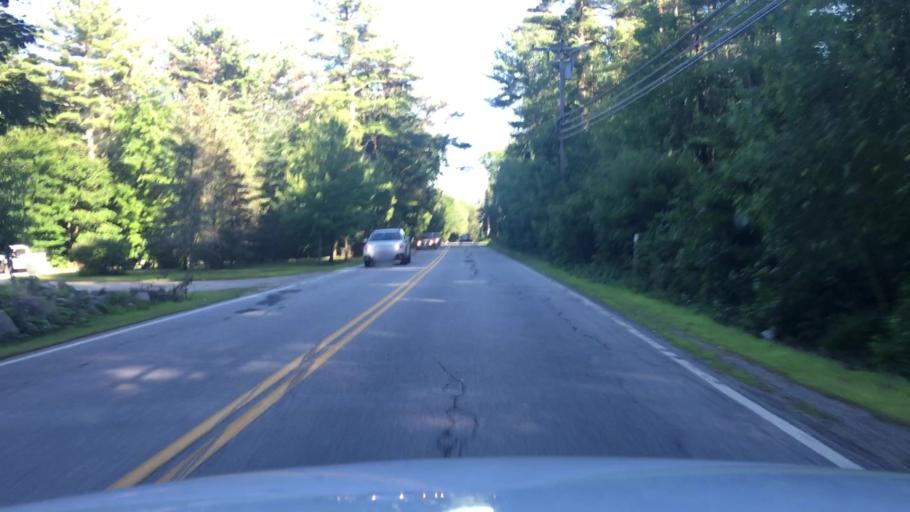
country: US
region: New Hampshire
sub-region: Rockingham County
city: Danville
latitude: 42.9086
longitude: -71.1585
